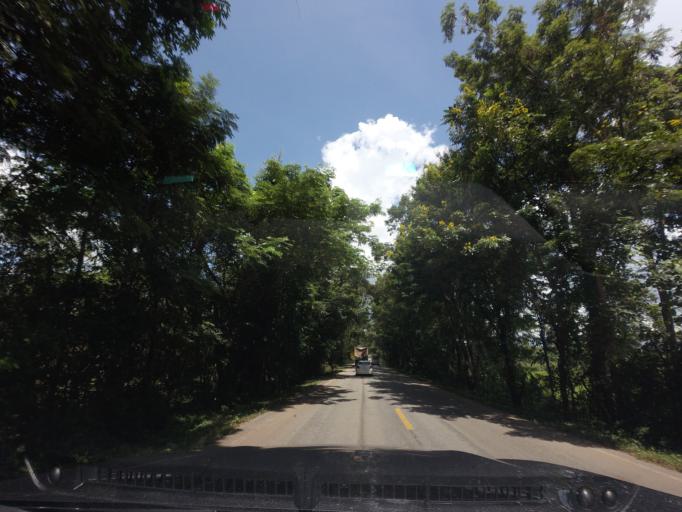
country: TH
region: Changwat Udon Thani
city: Phibun Rak
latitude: 17.5854
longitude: 103.0428
